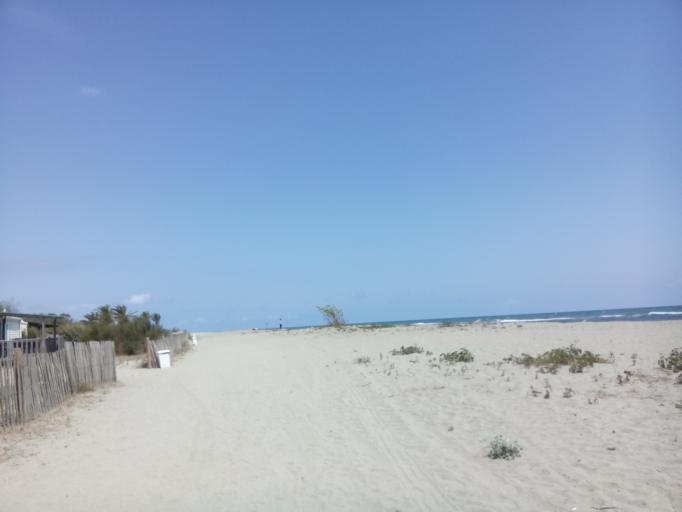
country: FR
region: Corsica
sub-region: Departement de la Haute-Corse
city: Aleria
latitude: 42.1056
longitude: 9.5490
